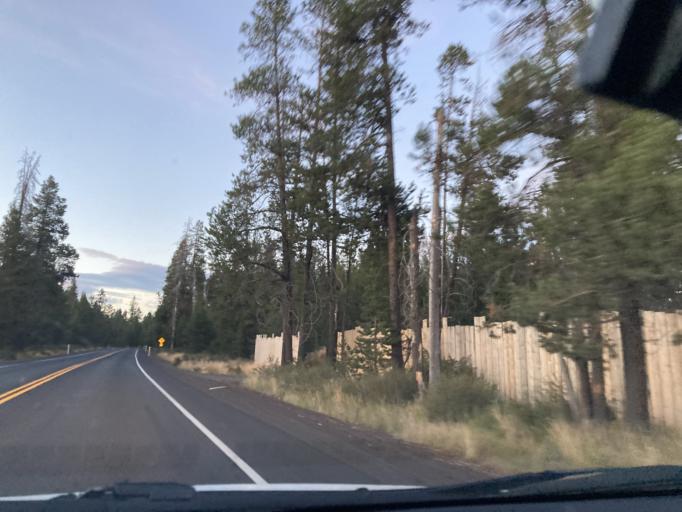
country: US
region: Oregon
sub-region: Deschutes County
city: Three Rivers
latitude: 43.8263
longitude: -121.4421
